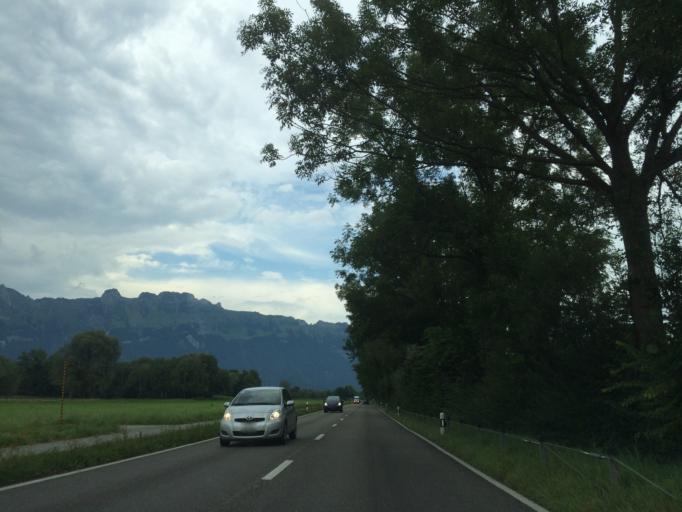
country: LI
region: Schaan
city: Schaan
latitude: 47.1875
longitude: 9.5051
